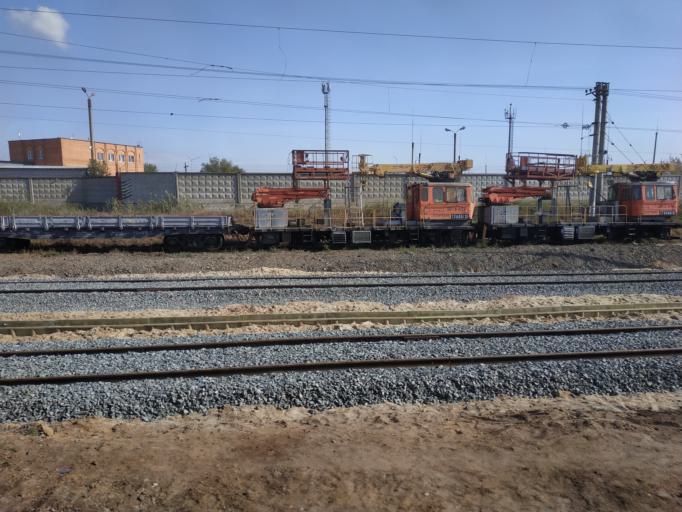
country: RU
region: Volgograd
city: Gumrak
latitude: 48.7744
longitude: 44.3826
